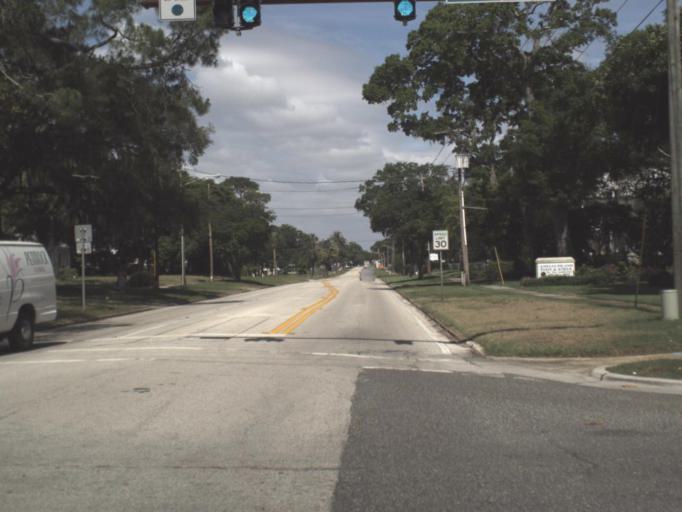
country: US
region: Florida
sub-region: Nassau County
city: Fernandina Beach
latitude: 30.6699
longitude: -81.4514
